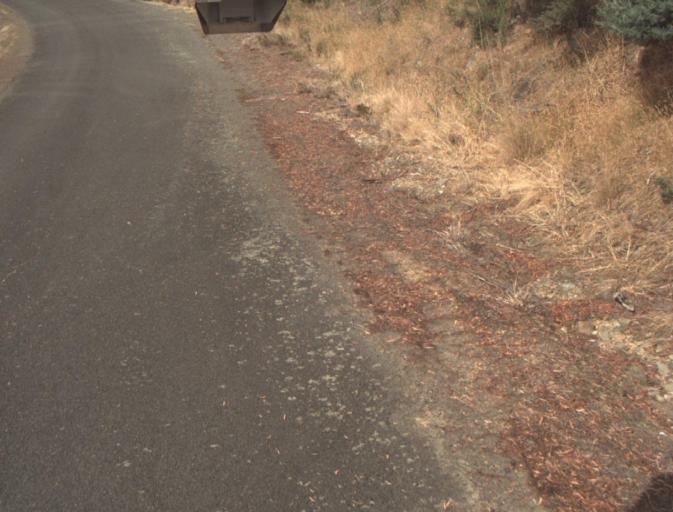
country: AU
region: Tasmania
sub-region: Northern Midlands
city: Evandale
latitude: -41.4785
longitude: 147.5005
